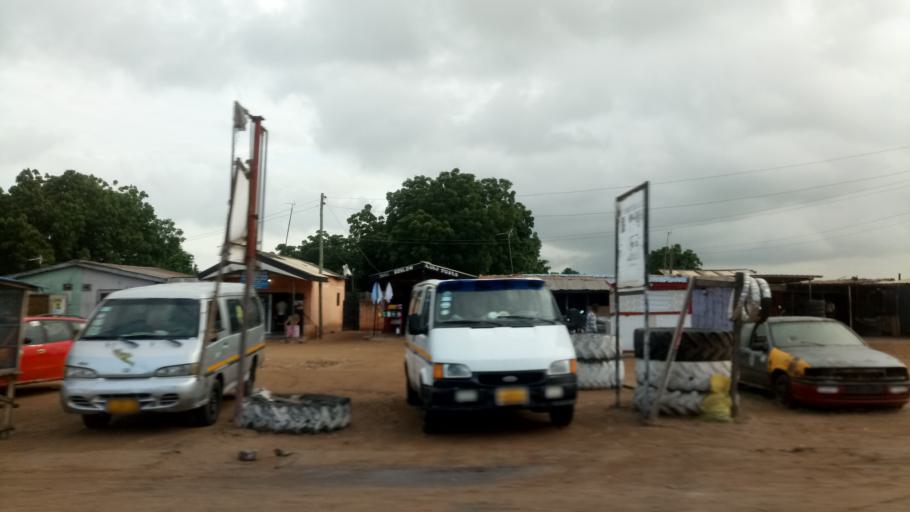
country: GH
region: Greater Accra
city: Tema
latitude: 5.8751
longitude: 0.3620
